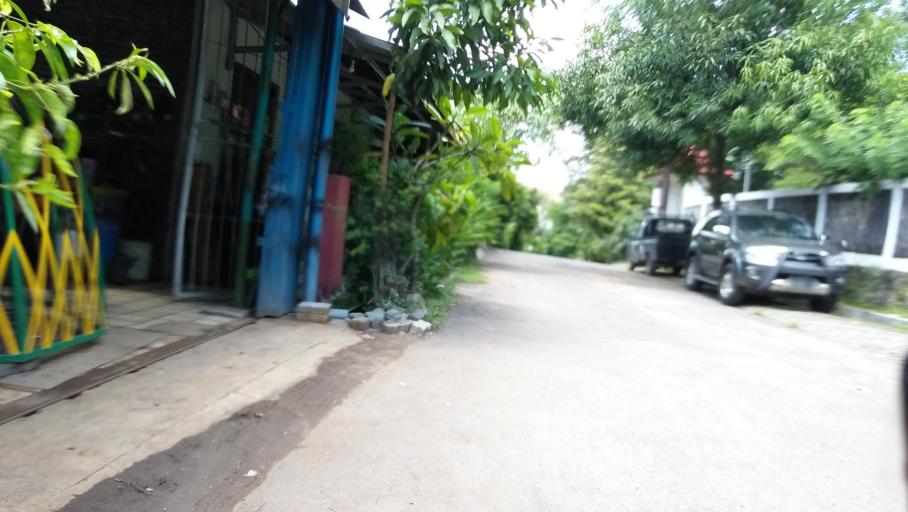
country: ID
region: Central Java
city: Semarang
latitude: -7.0313
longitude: 110.4605
